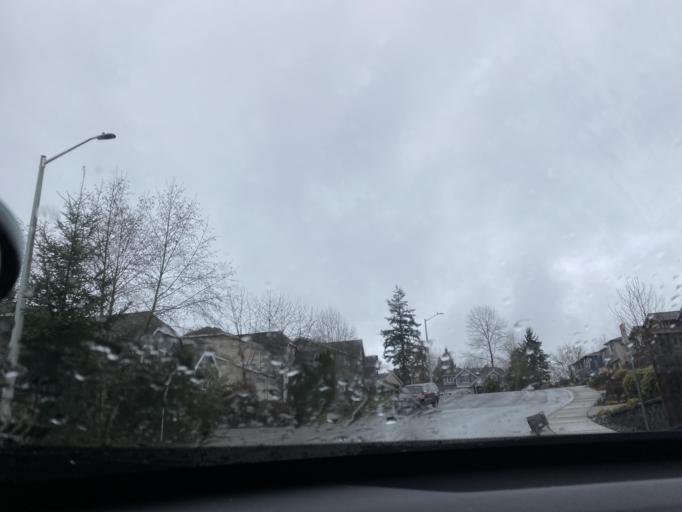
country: US
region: Washington
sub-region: Snohomish County
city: Alderwood Manor
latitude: 47.8087
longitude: -122.2949
